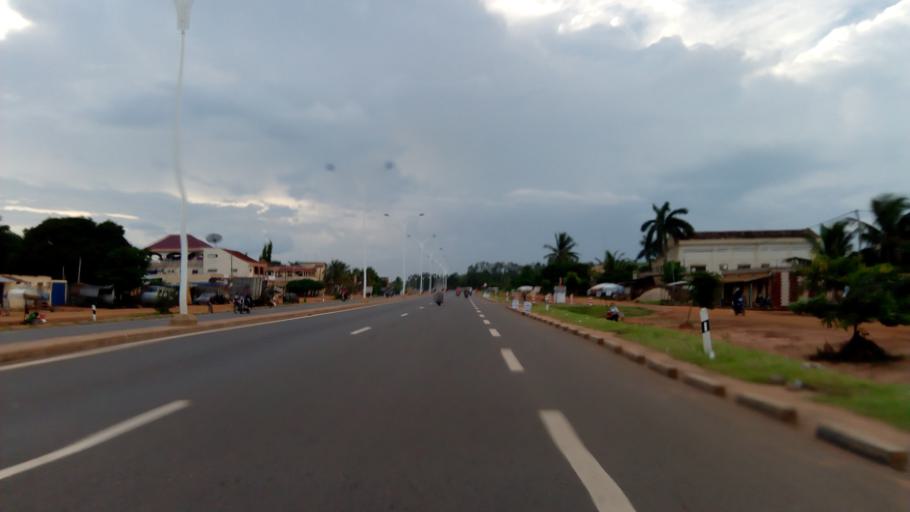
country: TG
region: Maritime
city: Lome
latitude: 6.2436
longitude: 1.1948
